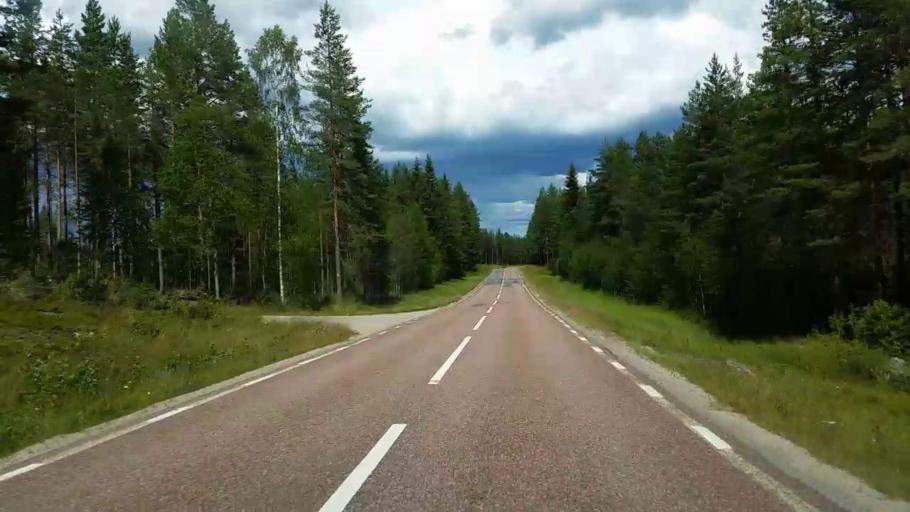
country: SE
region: Gaevleborg
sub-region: Ovanakers Kommun
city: Edsbyn
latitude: 61.3174
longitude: 15.5101
